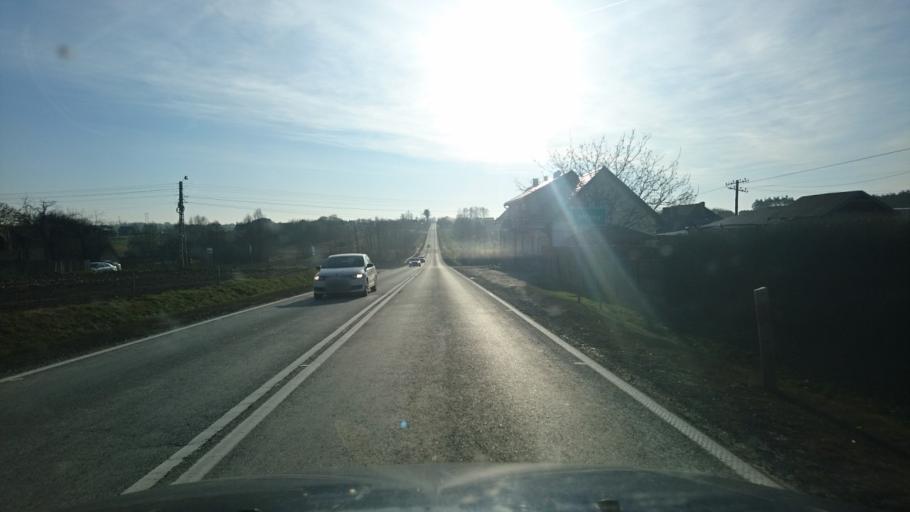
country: PL
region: Opole Voivodeship
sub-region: Powiat oleski
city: Dalachow
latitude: 51.0571
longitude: 18.5991
